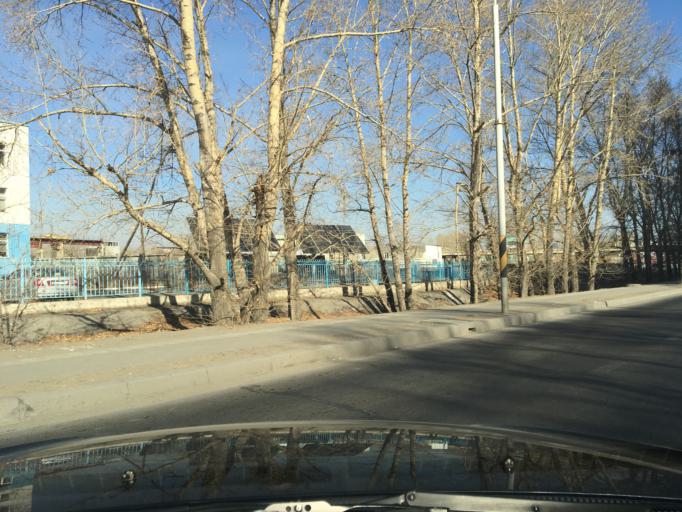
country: MN
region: Ulaanbaatar
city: Ulaanbaatar
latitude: 47.8924
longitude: 106.8740
